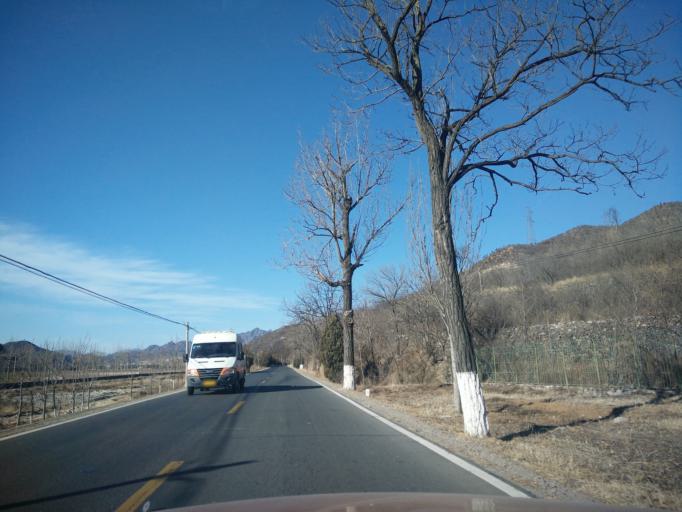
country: CN
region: Beijing
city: Zhaitang
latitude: 39.9859
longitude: 115.7327
